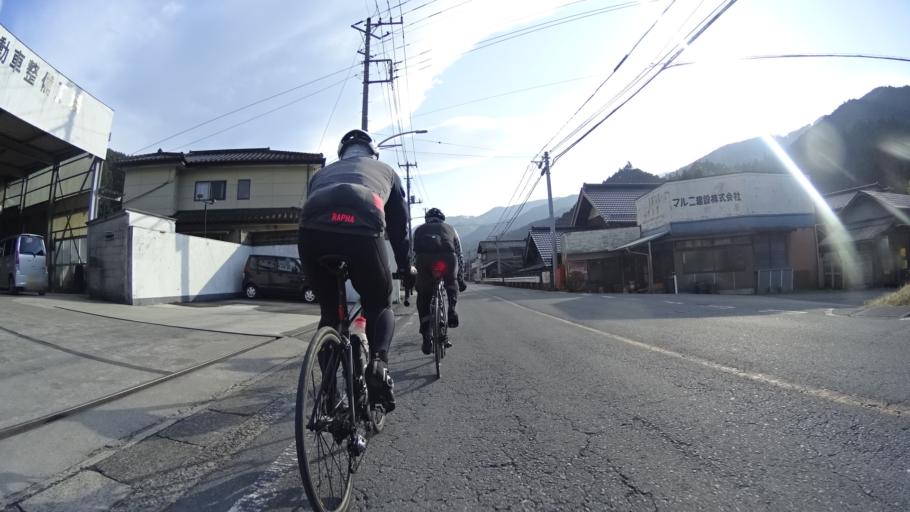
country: JP
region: Tokyo
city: Ome
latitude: 35.8696
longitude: 139.1869
